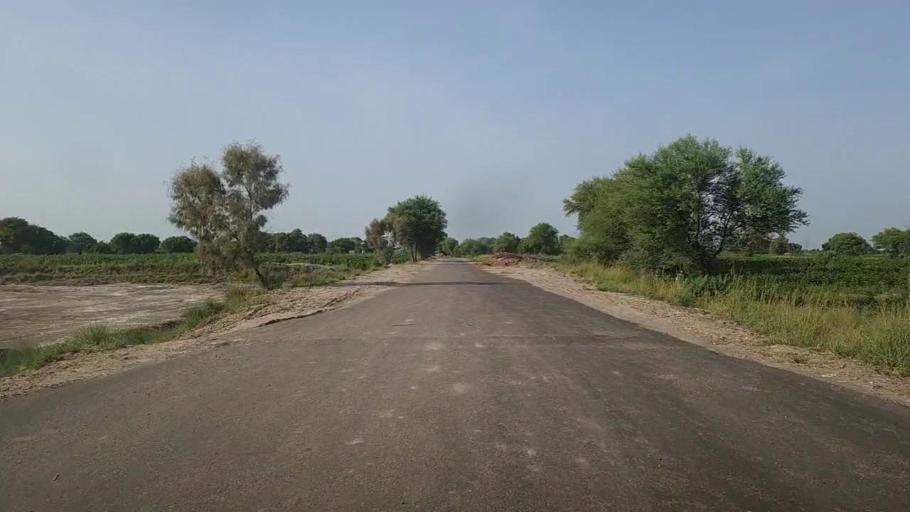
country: PK
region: Sindh
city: Ubauro
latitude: 28.0891
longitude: 69.8439
